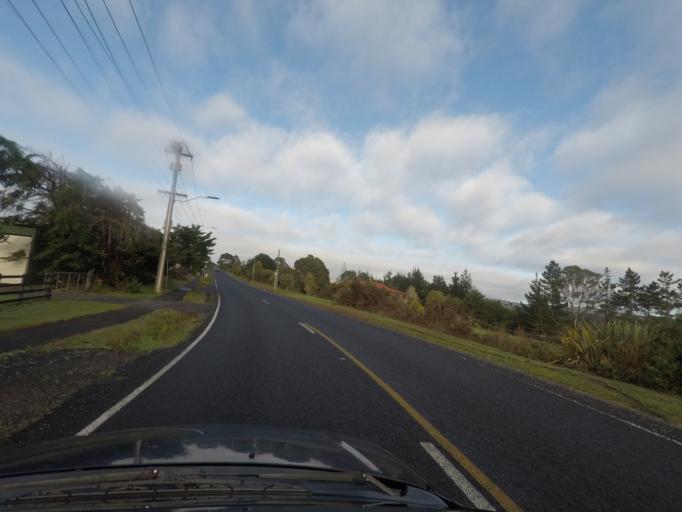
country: NZ
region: Auckland
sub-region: Auckland
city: Waitakere
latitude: -36.9008
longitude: 174.6145
